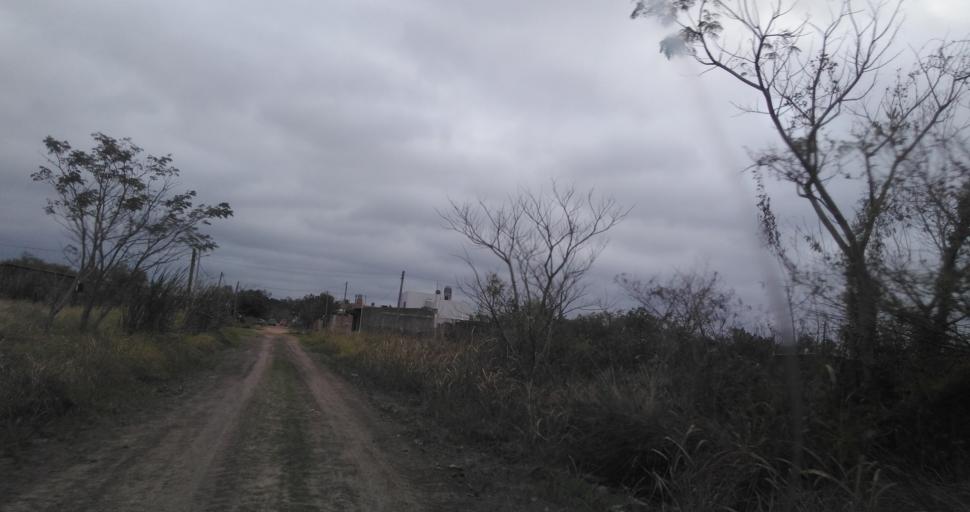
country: AR
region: Chaco
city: Fontana
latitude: -27.4475
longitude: -59.0293
